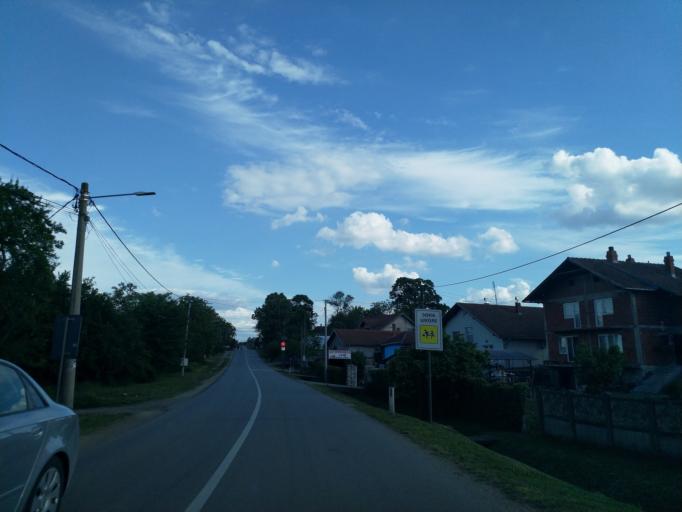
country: RS
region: Central Serbia
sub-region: Sumadijski Okrug
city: Lapovo
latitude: 44.1704
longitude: 21.0921
